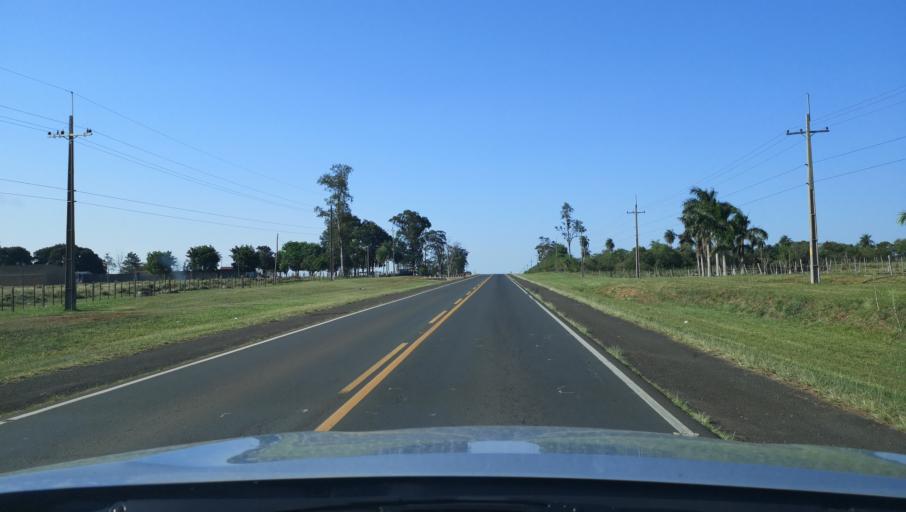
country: PY
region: Misiones
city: Santa Maria
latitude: -26.8252
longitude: -57.0286
